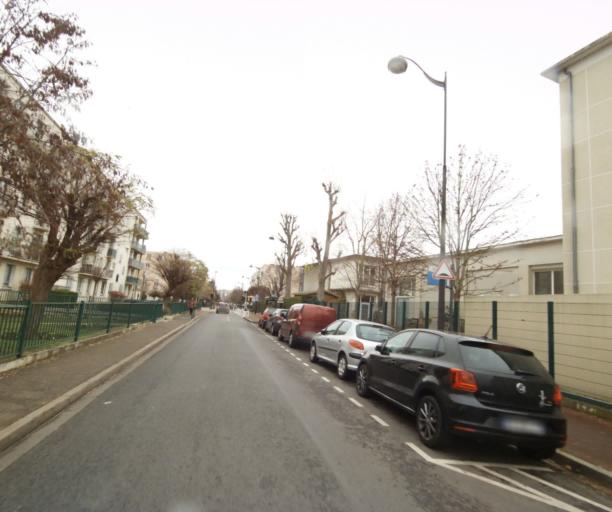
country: FR
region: Ile-de-France
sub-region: Departement des Yvelines
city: Chatou
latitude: 48.8838
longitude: 2.1705
